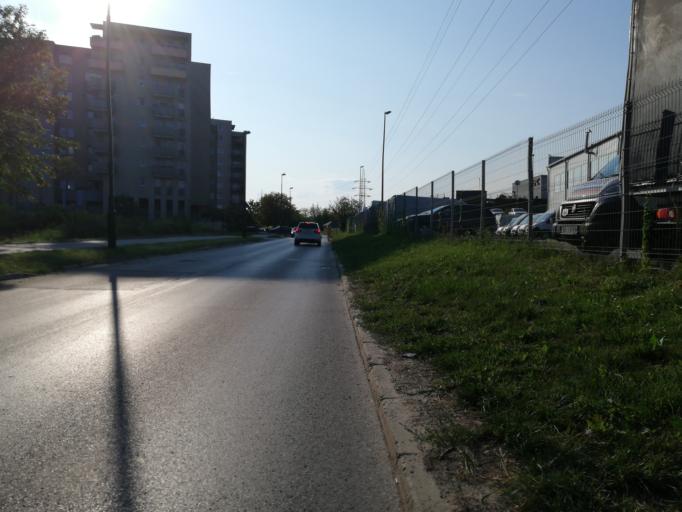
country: PL
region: Lesser Poland Voivodeship
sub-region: Krakow
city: Krakow
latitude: 50.0865
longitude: 20.0062
